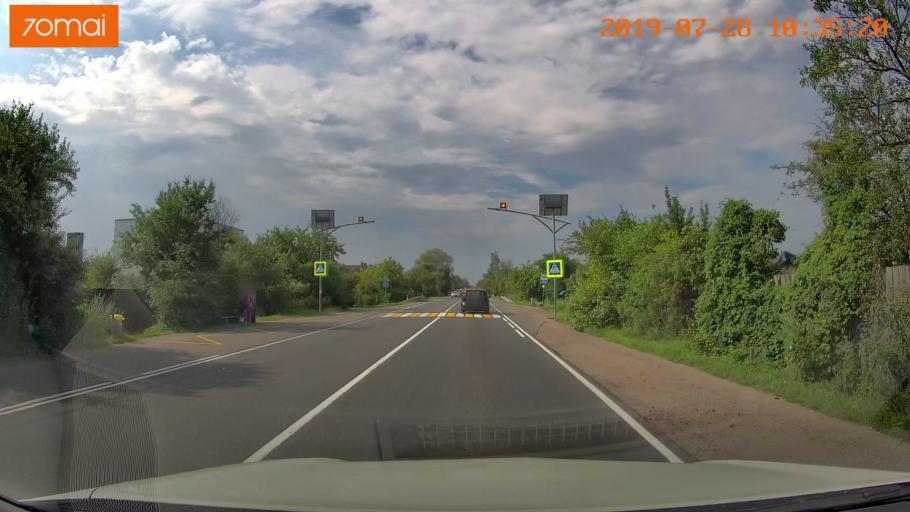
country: RU
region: Kaliningrad
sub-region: Gorod Kaliningrad
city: Kaliningrad
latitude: 54.7476
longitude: 20.4324
